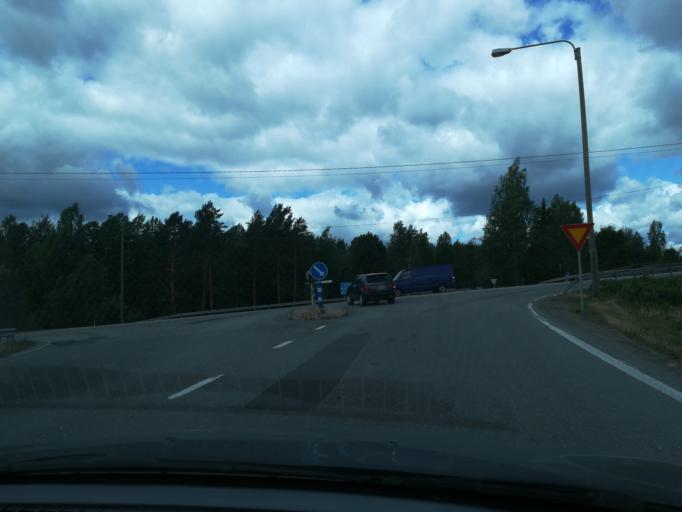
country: FI
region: Southern Savonia
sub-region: Mikkeli
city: Ristiina
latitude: 61.5132
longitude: 27.2423
